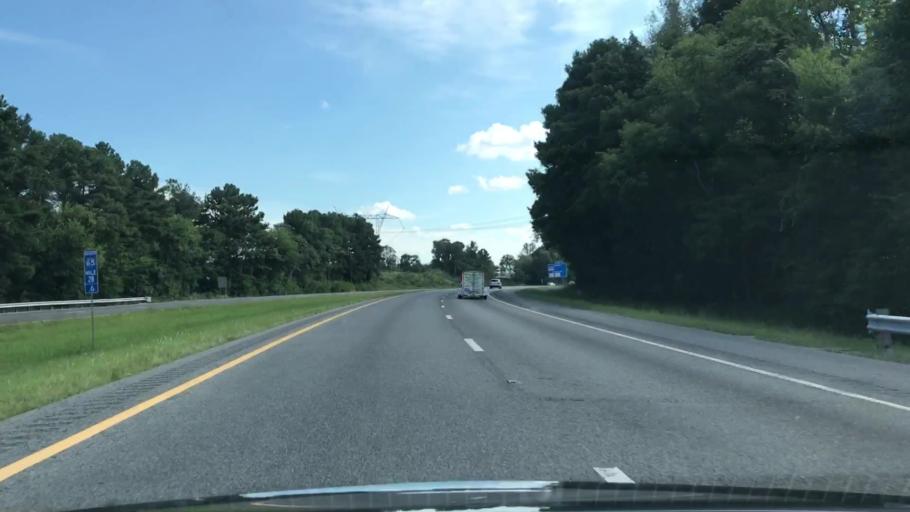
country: US
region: Tennessee
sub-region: Marshall County
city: Cornersville
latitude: 35.3940
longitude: -86.8790
